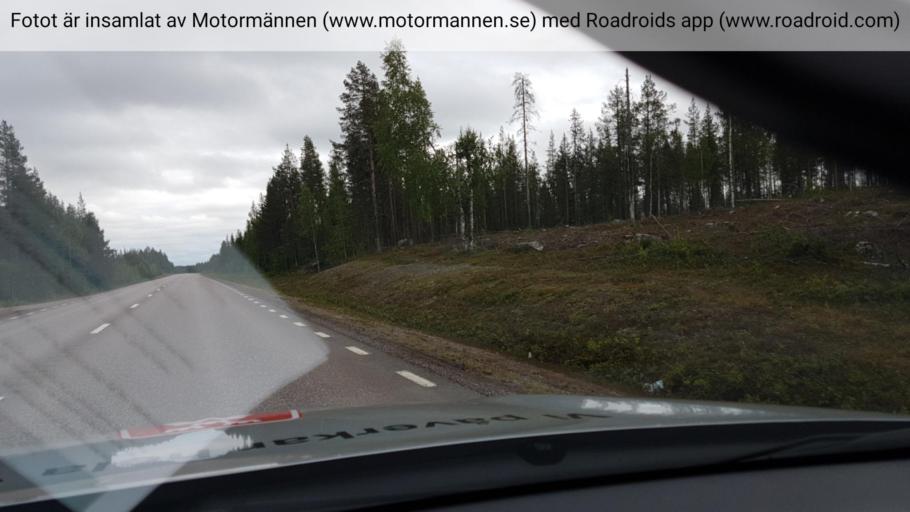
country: SE
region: Norrbotten
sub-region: Gallivare Kommun
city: Gaellivare
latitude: 67.0729
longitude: 21.1015
